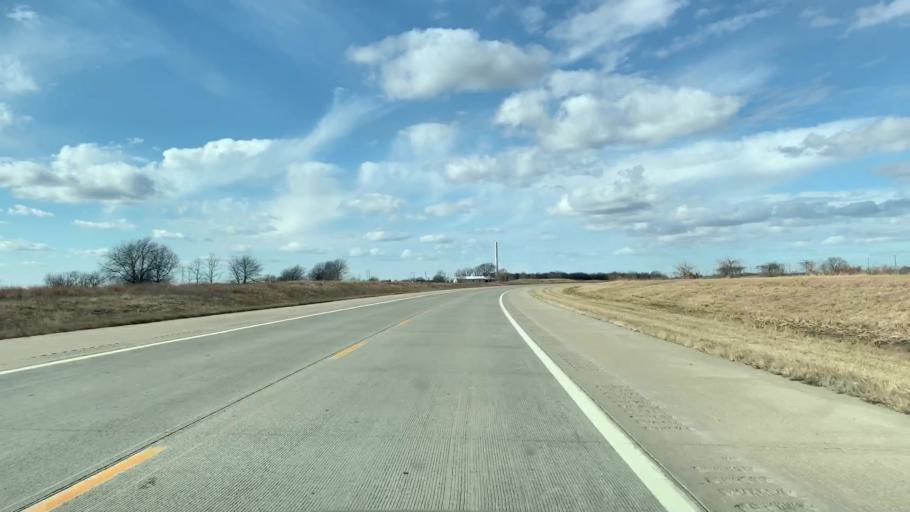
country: US
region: Kansas
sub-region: Labette County
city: Parsons
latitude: 37.3516
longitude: -95.2061
